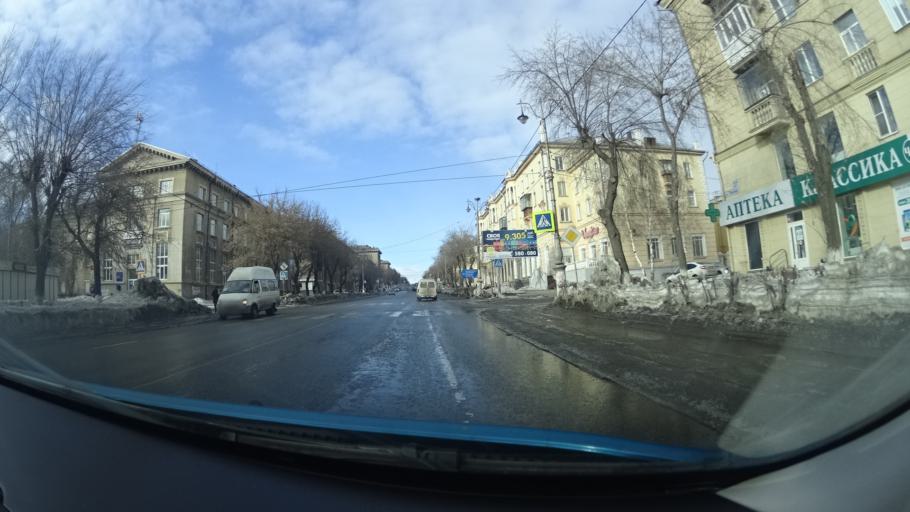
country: RU
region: Chelyabinsk
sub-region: Gorod Magnitogorsk
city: Magnitogorsk
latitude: 53.4243
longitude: 58.9837
